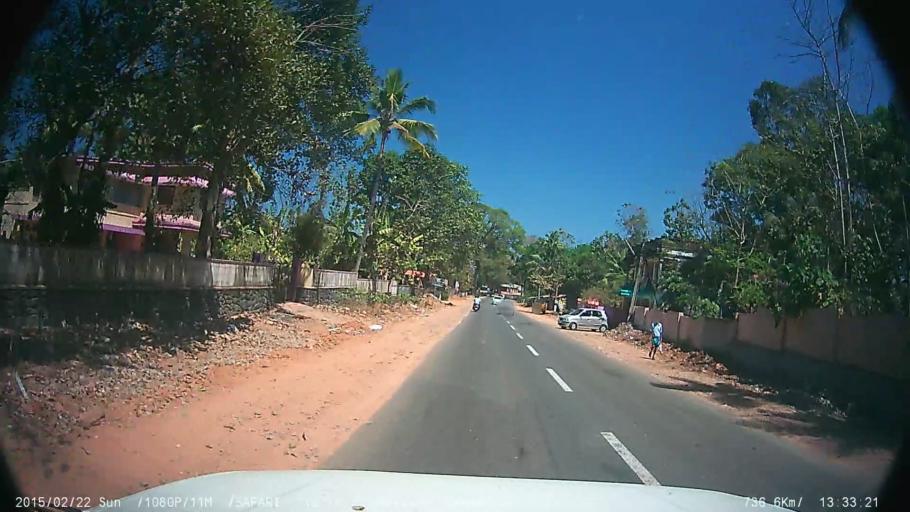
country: IN
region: Kerala
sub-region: Kottayam
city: Changanacheri
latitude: 9.4807
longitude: 76.5913
